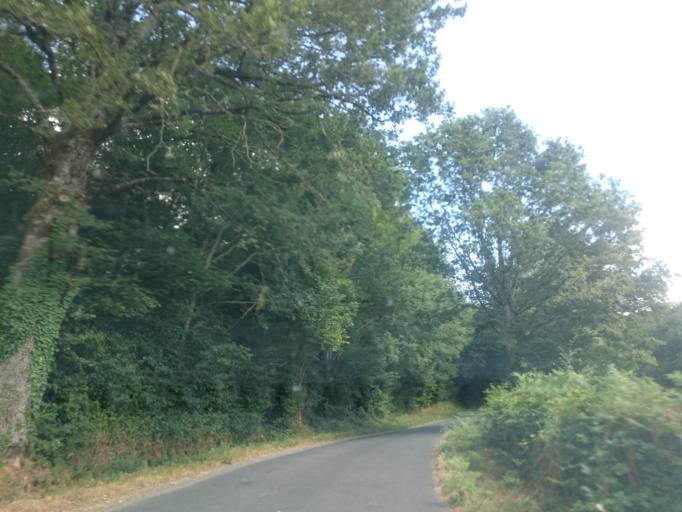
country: FR
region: Auvergne
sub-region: Departement du Cantal
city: Laroquebrou
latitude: 44.8970
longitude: 2.2067
